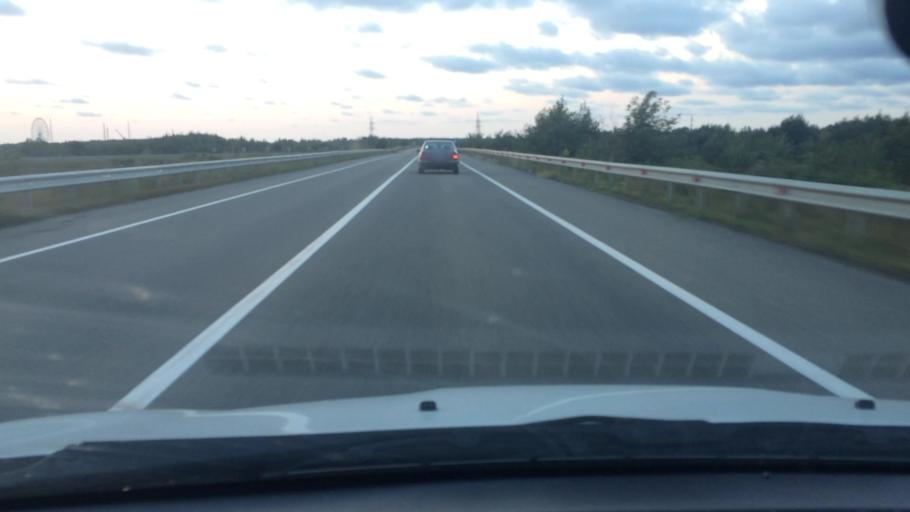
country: GE
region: Ajaria
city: Ochkhamuri
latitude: 41.9011
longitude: 41.7941
